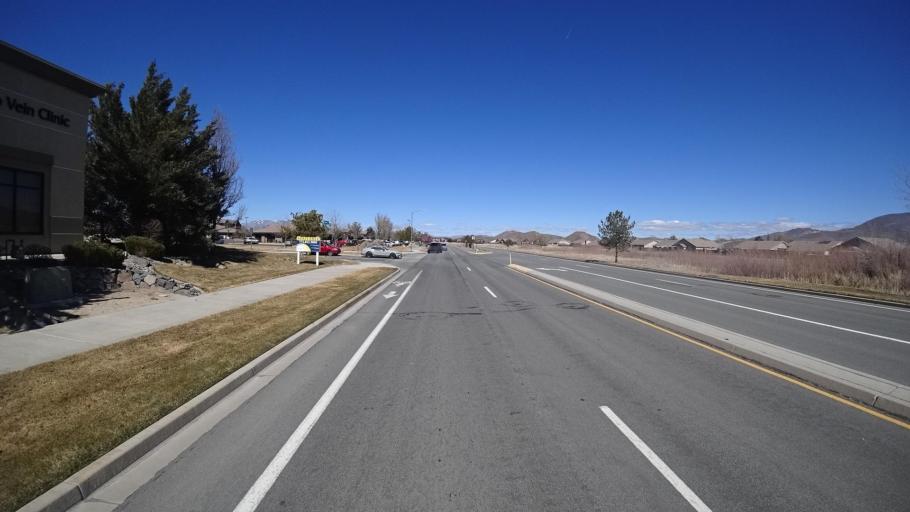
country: US
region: Nevada
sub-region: Washoe County
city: Sparks
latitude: 39.4274
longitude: -119.7519
